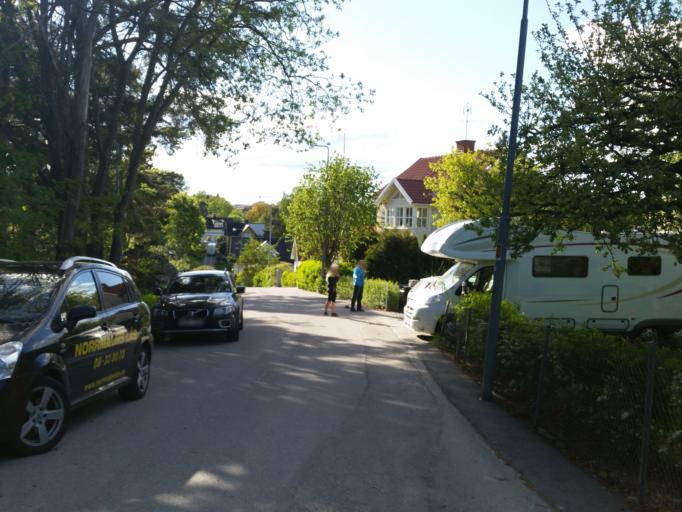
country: SE
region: Stockholm
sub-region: Sundbybergs Kommun
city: Sundbyberg
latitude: 59.3734
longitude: 17.9586
